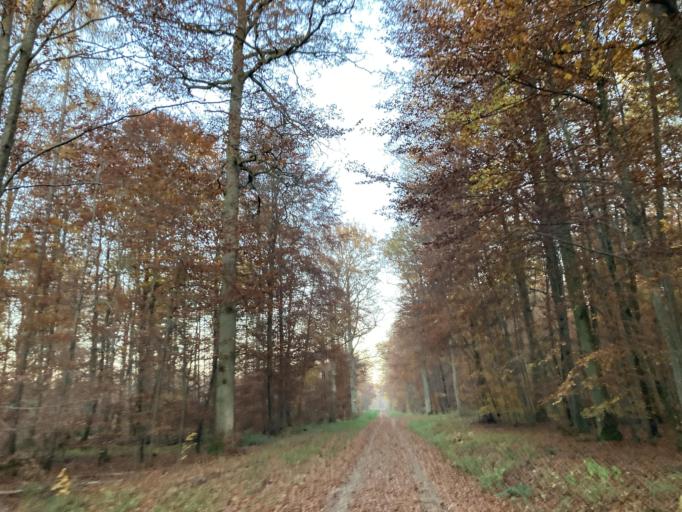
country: DE
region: Baden-Wuerttemberg
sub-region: Tuebingen Region
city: Dettenhausen
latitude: 48.5928
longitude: 9.0984
